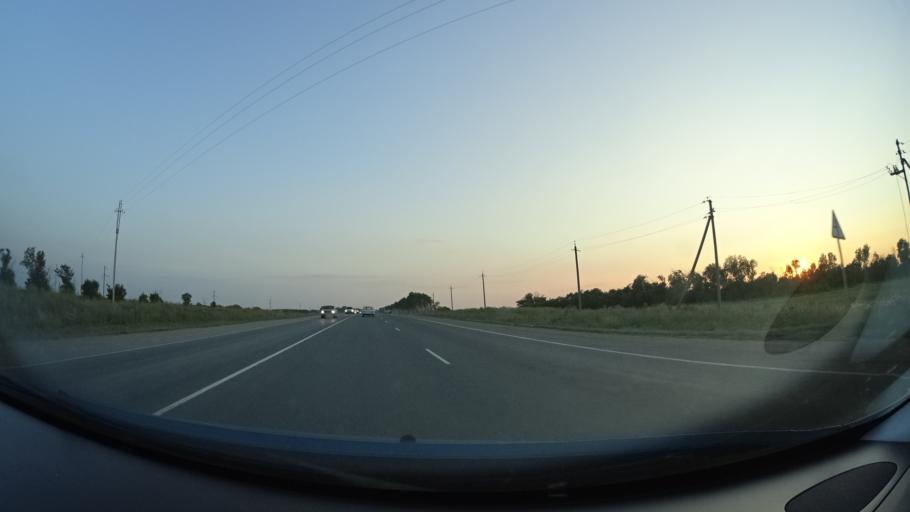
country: RU
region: Samara
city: Sukhodol
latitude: 53.8609
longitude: 51.1743
